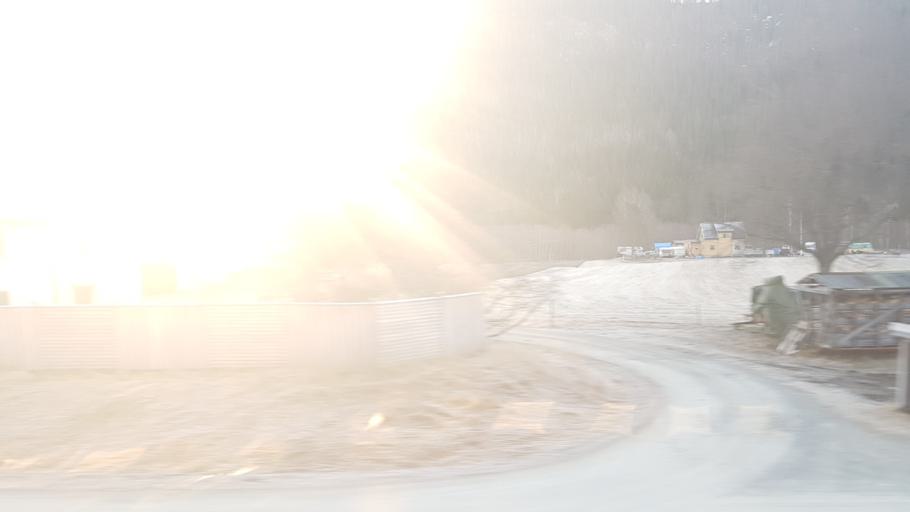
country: NO
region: Nord-Trondelag
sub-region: Stjordal
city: Stjordalshalsen
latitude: 63.5923
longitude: 11.0151
